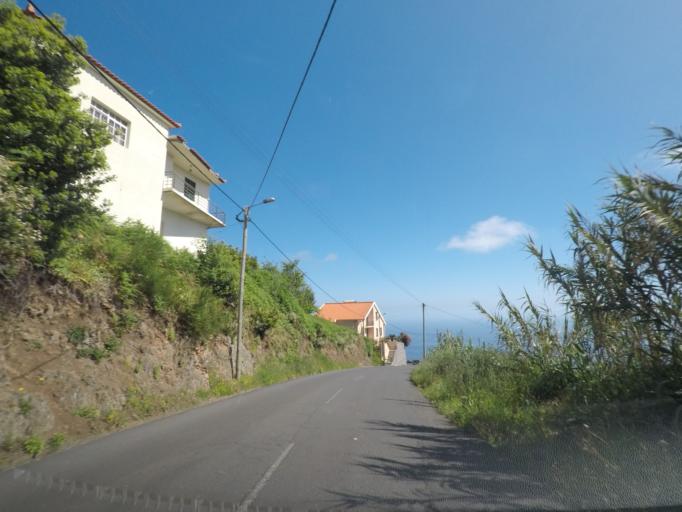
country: PT
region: Madeira
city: Ponta do Sol
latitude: 32.7038
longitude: -17.1118
